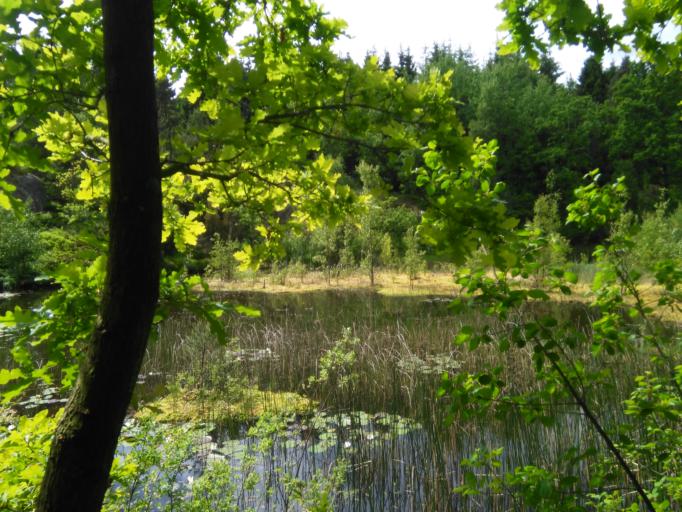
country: DK
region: Capital Region
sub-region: Bornholm Kommune
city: Nexo
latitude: 55.0956
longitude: 15.1028
